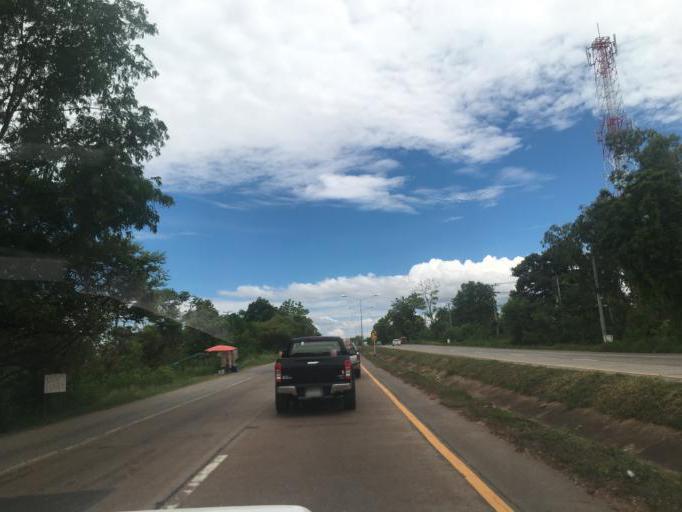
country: TH
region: Khon Kaen
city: Nam Phong
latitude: 16.6529
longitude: 102.8004
